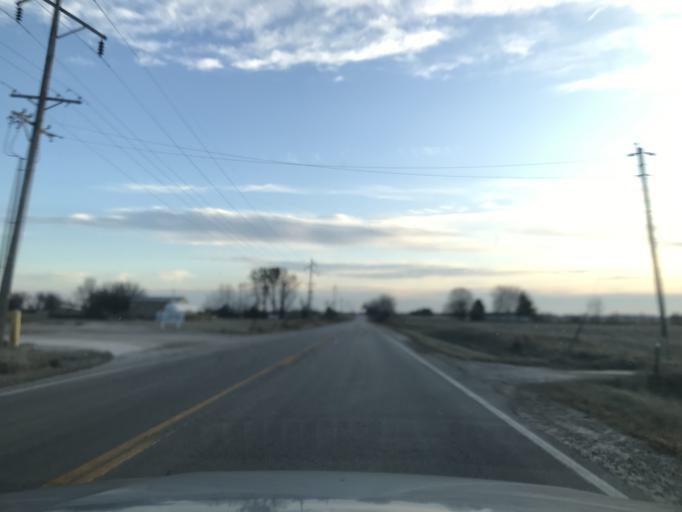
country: US
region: Illinois
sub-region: Warren County
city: Monmouth
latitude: 41.0341
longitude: -90.7461
